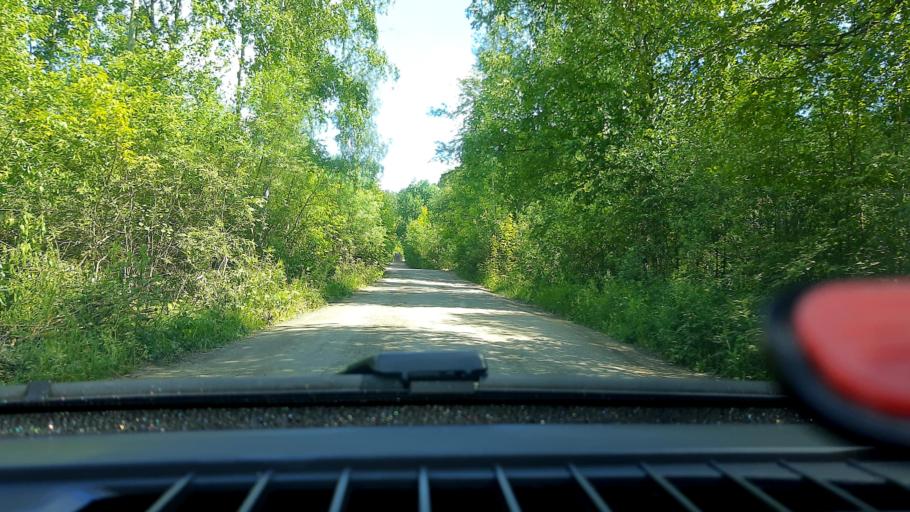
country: RU
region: Nizjnij Novgorod
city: Gorbatovka
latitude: 56.2989
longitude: 43.8215
